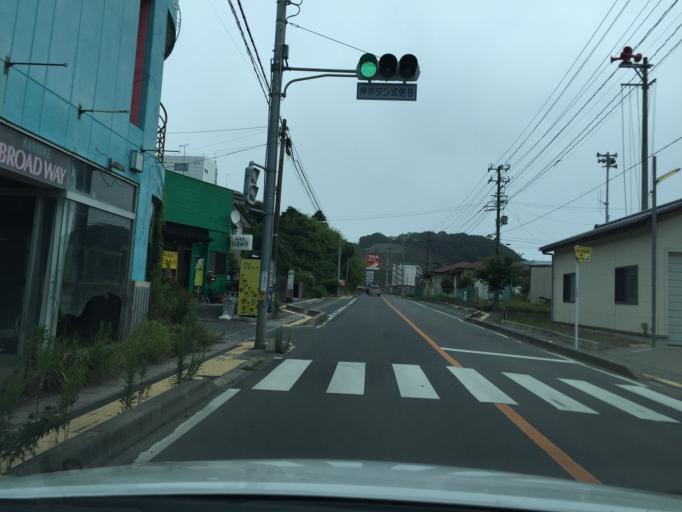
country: JP
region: Fukushima
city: Iwaki
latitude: 36.9491
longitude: 140.9251
